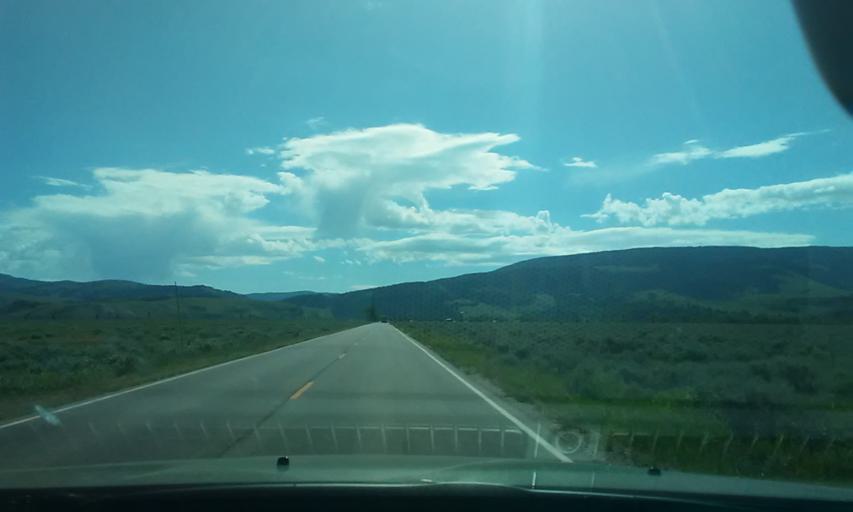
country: US
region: Wyoming
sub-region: Teton County
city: Jackson
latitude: 43.6251
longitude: -110.6480
